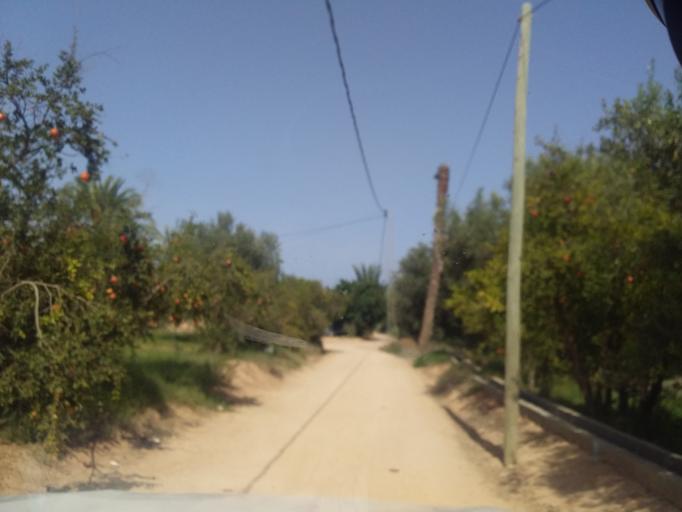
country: TN
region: Qabis
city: Gabes
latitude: 33.6264
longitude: 10.2918
